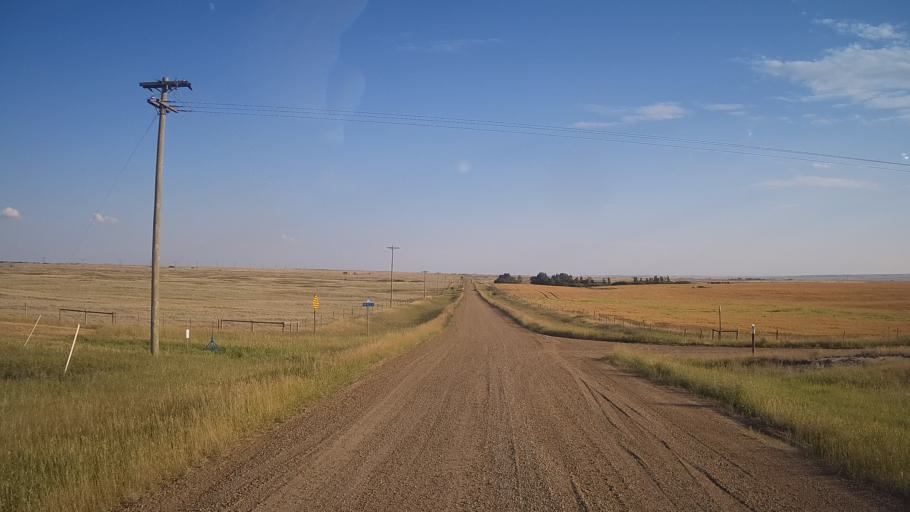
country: CA
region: Alberta
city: Hanna
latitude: 51.6202
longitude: -111.8570
